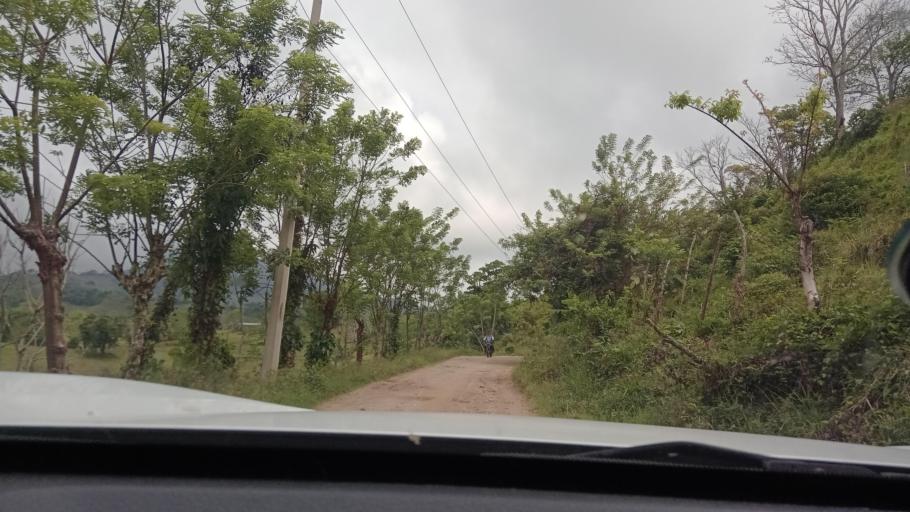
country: MX
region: Tabasco
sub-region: Huimanguillo
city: Francisco Rueda
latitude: 17.5200
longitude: -94.1236
